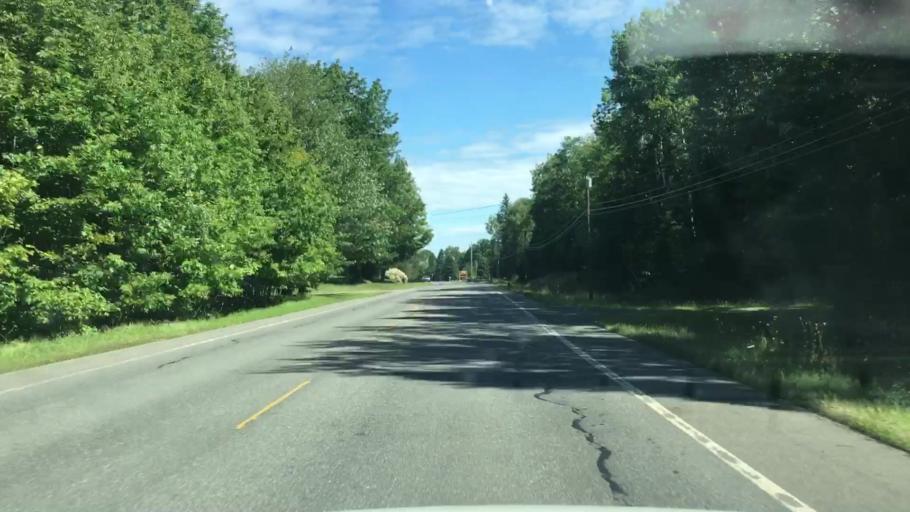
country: US
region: Maine
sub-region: Penobscot County
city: Dexter
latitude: 45.0673
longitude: -69.2411
